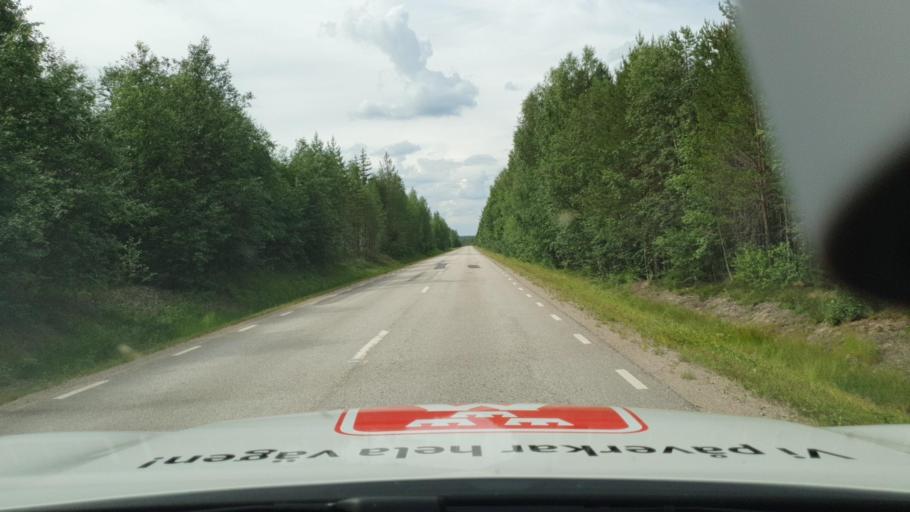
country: NO
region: Hedmark
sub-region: Trysil
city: Innbygda
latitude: 60.9176
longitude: 12.5407
